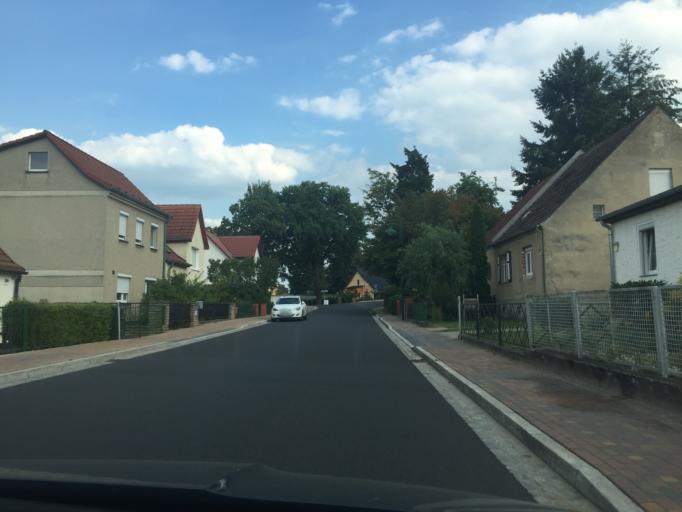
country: DE
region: Brandenburg
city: Erkner
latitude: 52.3864
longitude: 13.7485
